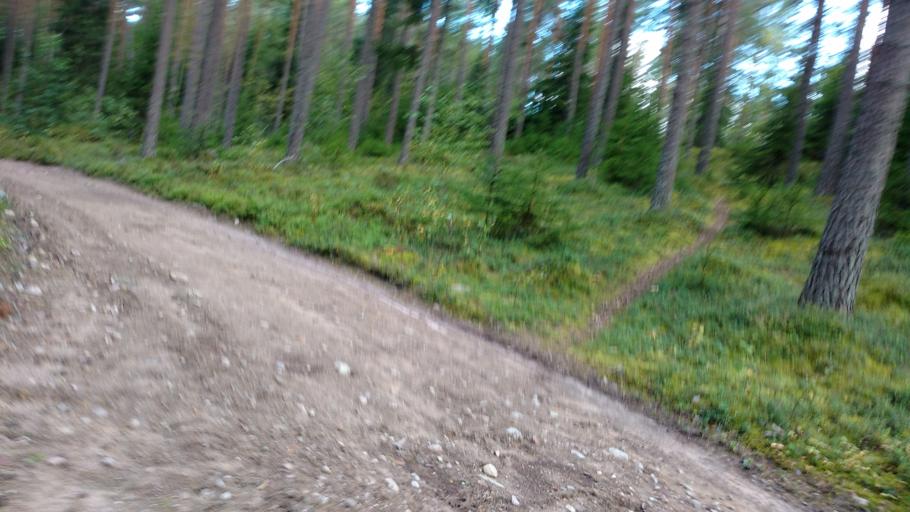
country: FI
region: Varsinais-Suomi
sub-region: Salo
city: Salo
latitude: 60.3571
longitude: 23.1577
